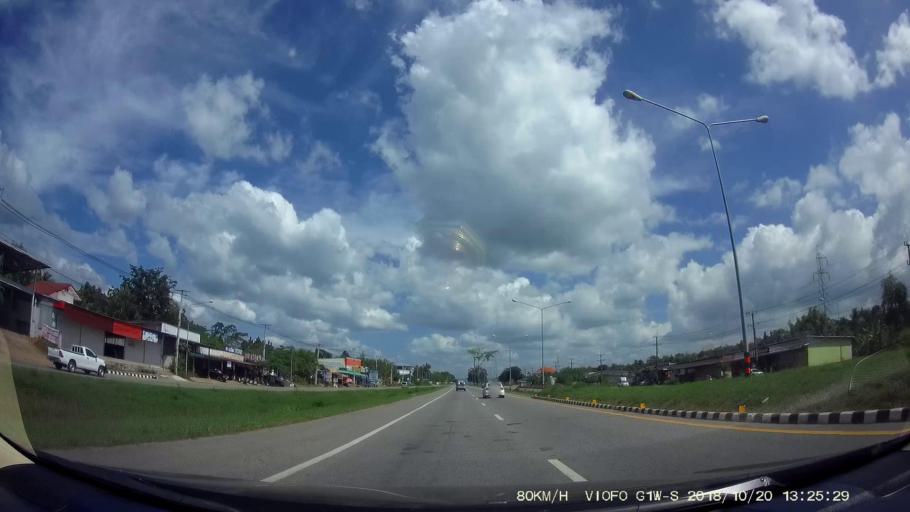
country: TH
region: Chaiyaphum
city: Khon San
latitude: 16.5949
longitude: 101.9328
